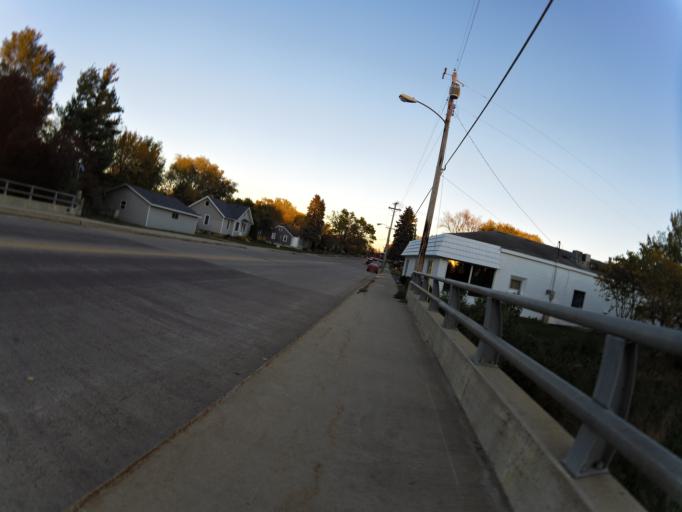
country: US
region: Minnesota
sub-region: Olmsted County
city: Rochester
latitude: 44.0306
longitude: -92.4718
